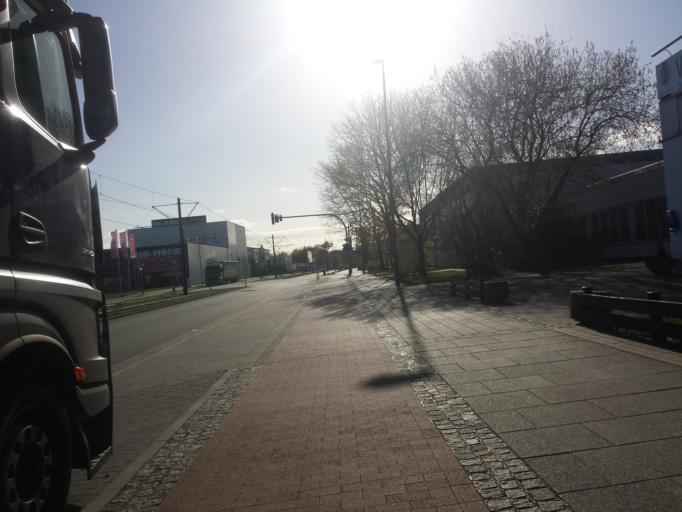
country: DE
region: Lower Saxony
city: Oyten
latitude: 53.0458
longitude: 8.9561
